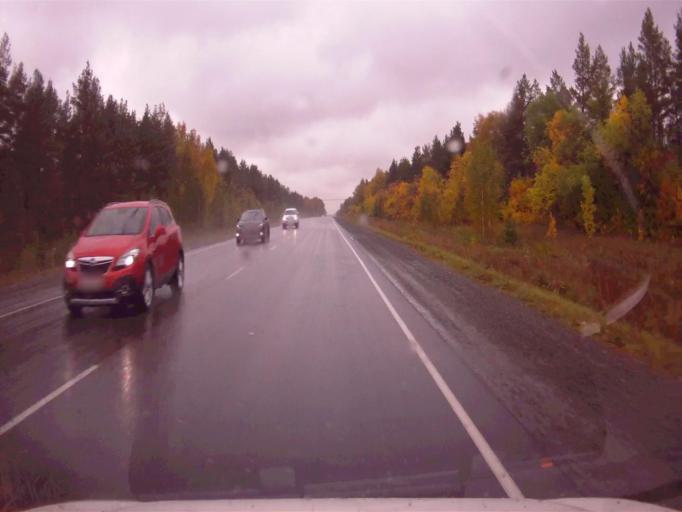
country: RU
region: Chelyabinsk
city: Roshchino
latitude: 55.3789
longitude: 61.1447
